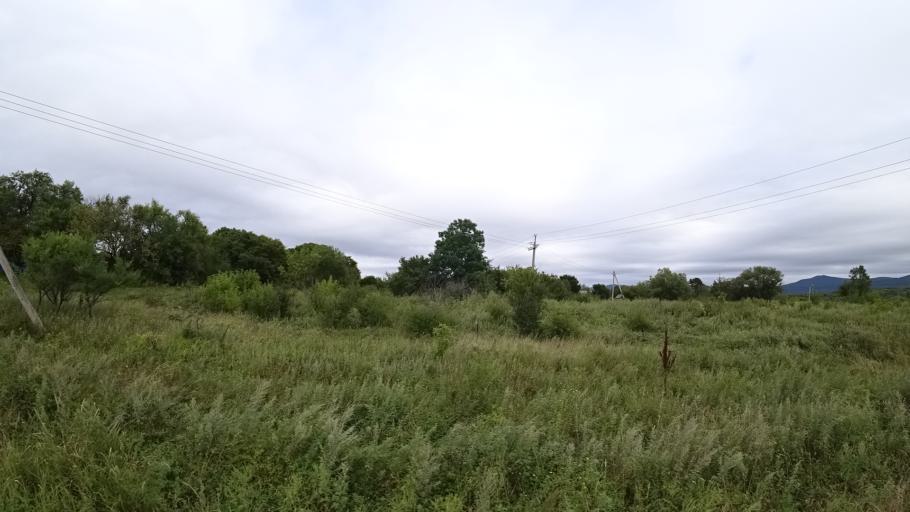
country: RU
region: Primorskiy
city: Rettikhovka
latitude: 44.1324
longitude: 132.6342
